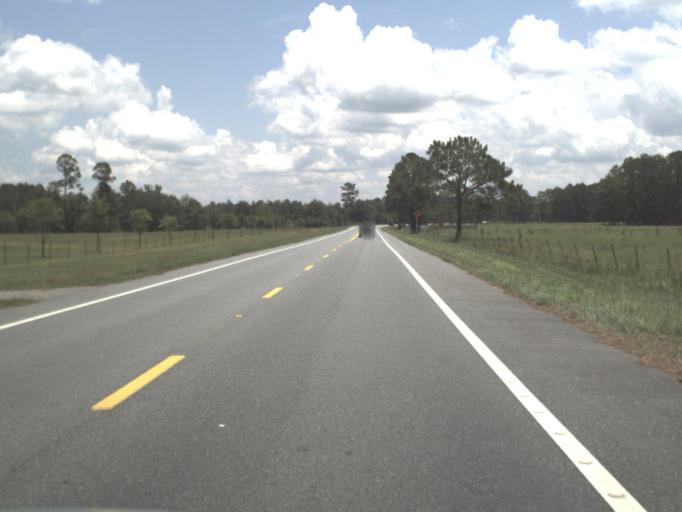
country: US
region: Florida
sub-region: Union County
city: Lake Butler
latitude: 30.0186
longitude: -82.4107
